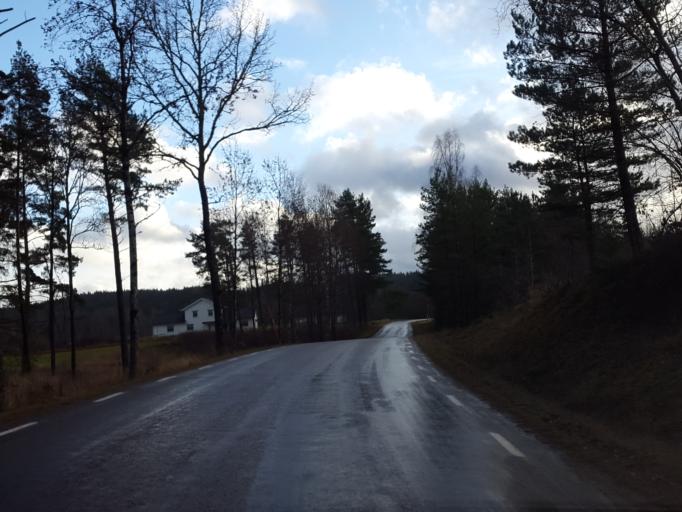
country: SE
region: Vaestra Goetaland
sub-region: Vargarda Kommun
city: Jonstorp
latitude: 57.9609
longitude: 12.7308
